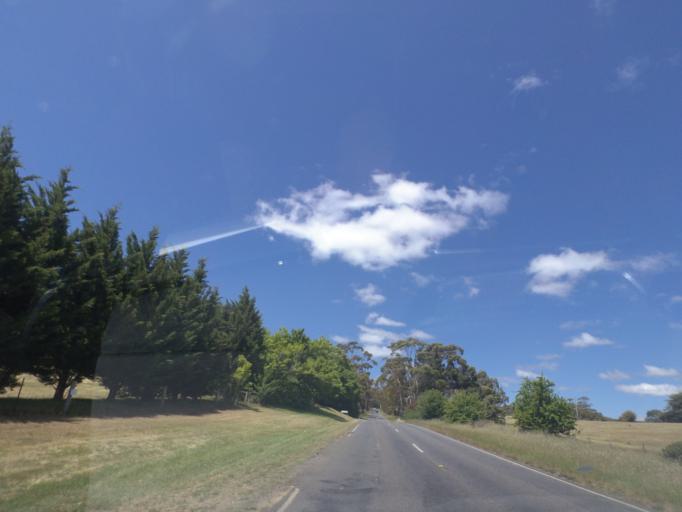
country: AU
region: Victoria
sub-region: Mount Alexander
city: Castlemaine
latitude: -37.2913
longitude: 144.2578
